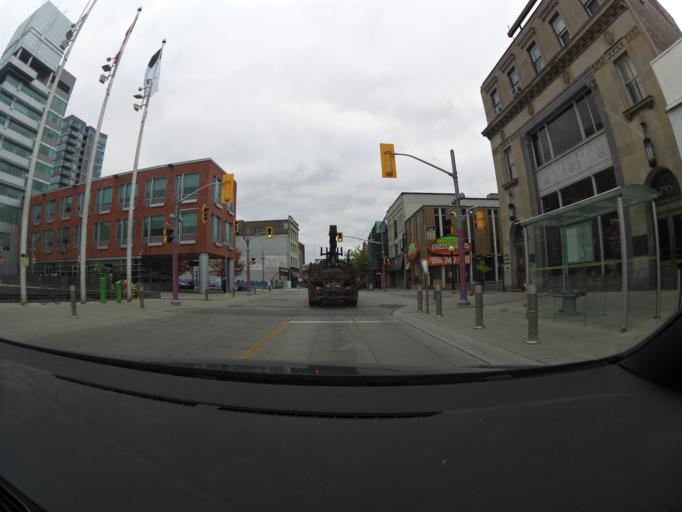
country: CA
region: Ontario
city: Waterloo
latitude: 43.4511
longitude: -80.4928
